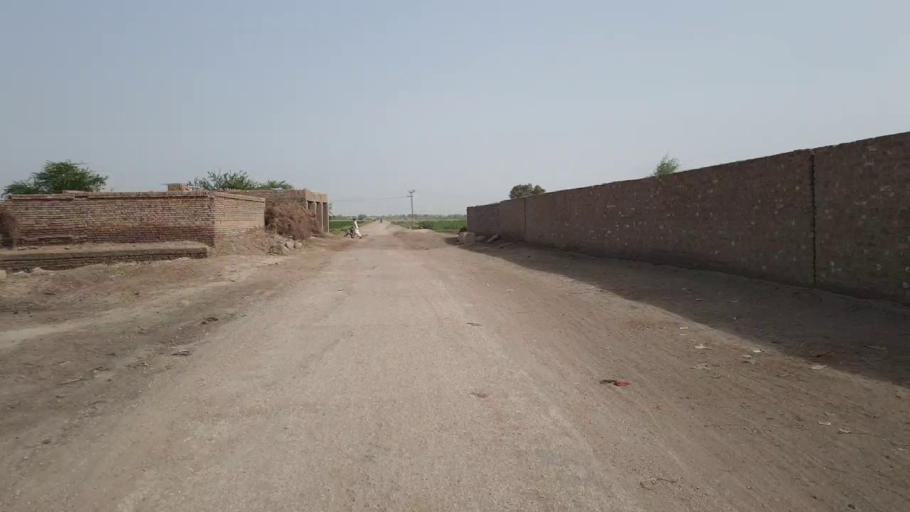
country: PK
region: Sindh
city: Daulatpur
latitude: 26.5552
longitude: 67.9900
